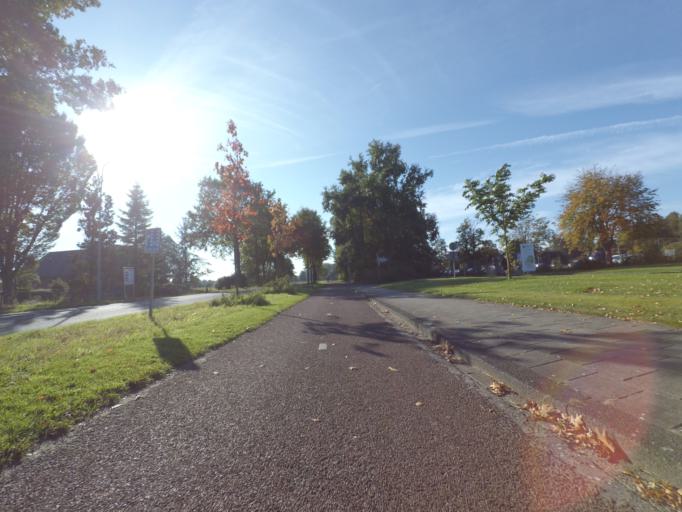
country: NL
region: Gelderland
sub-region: Gemeente Nijkerk
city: Nijkerk
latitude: 52.2174
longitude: 5.5020
